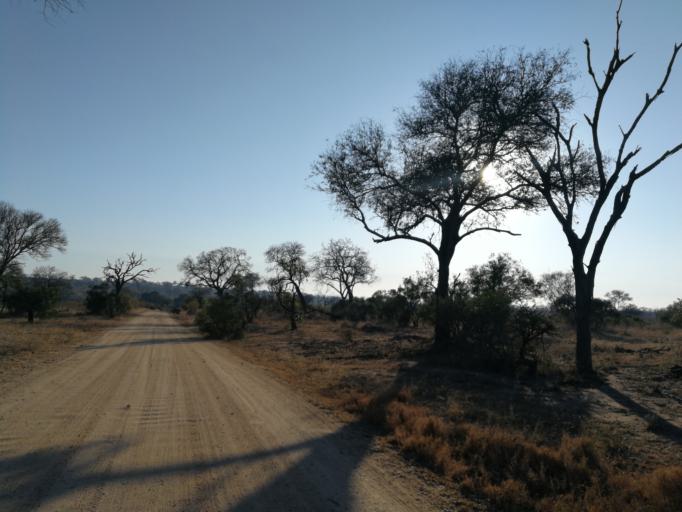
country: ZA
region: Limpopo
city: Thulamahashi
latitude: -25.0144
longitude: 31.4284
